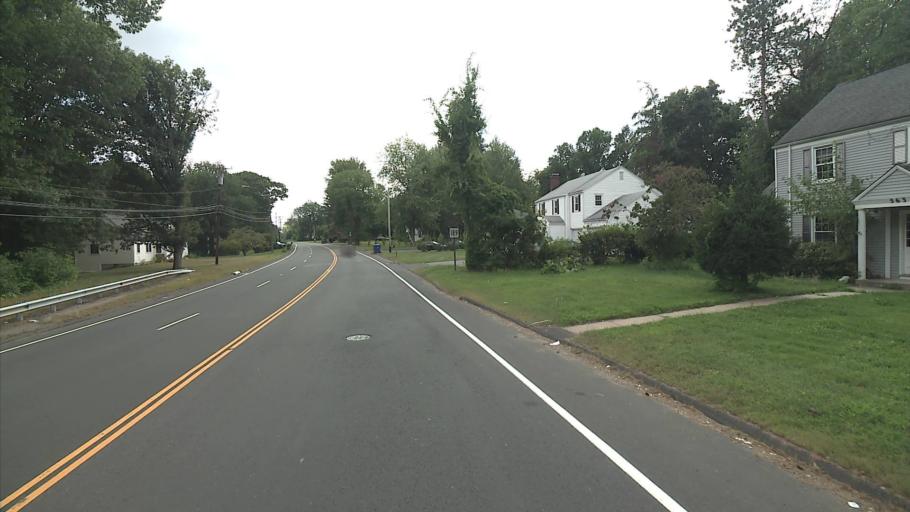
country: US
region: Connecticut
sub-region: Hartford County
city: Blue Hills
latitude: 41.8158
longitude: -72.7381
